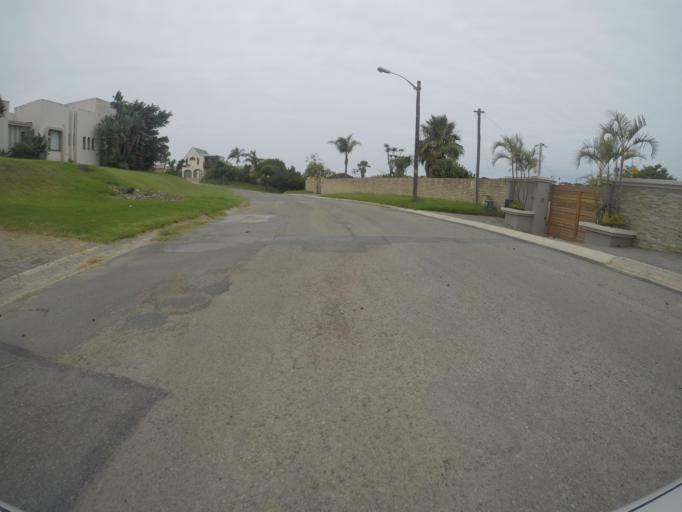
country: ZA
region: Eastern Cape
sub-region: Buffalo City Metropolitan Municipality
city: East London
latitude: -32.9805
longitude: 27.9346
